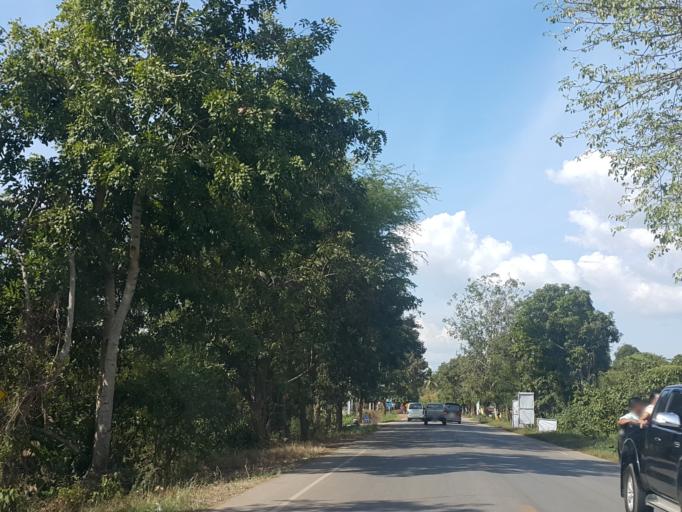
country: TH
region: Sukhothai
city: Sawankhalok
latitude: 17.2897
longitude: 99.8328
